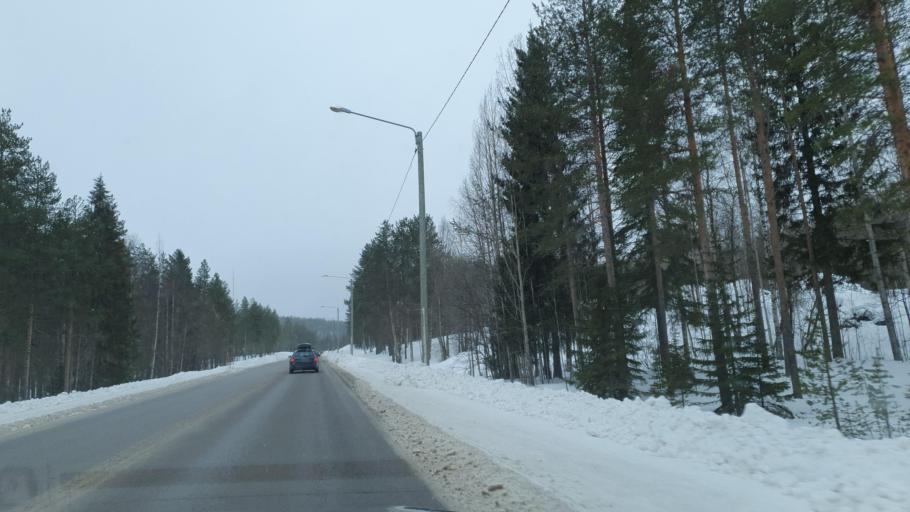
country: FI
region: Lapland
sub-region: Torniolaakso
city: Pello
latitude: 66.8974
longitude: 24.0918
